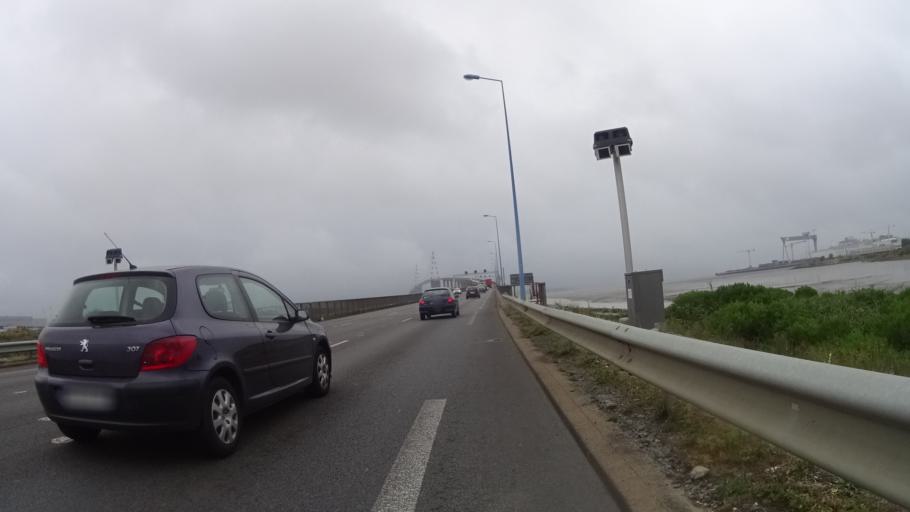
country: FR
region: Pays de la Loire
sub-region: Departement de la Loire-Atlantique
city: Trignac
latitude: 47.2974
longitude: -2.1783
